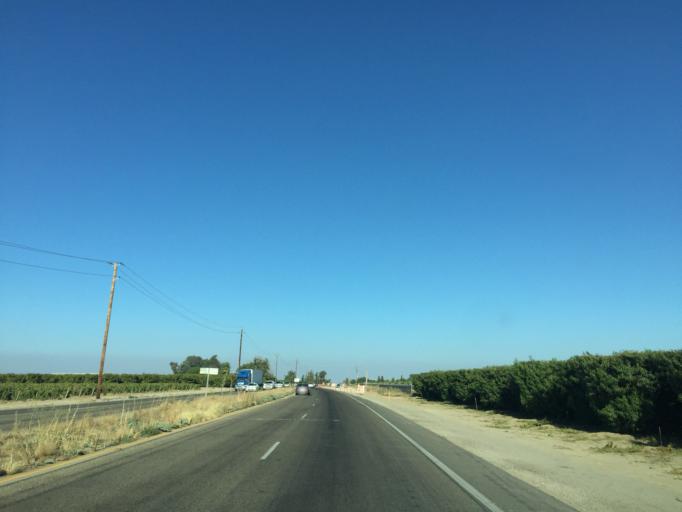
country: US
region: California
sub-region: Fresno County
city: Kingsburg
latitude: 36.5468
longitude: -119.5748
